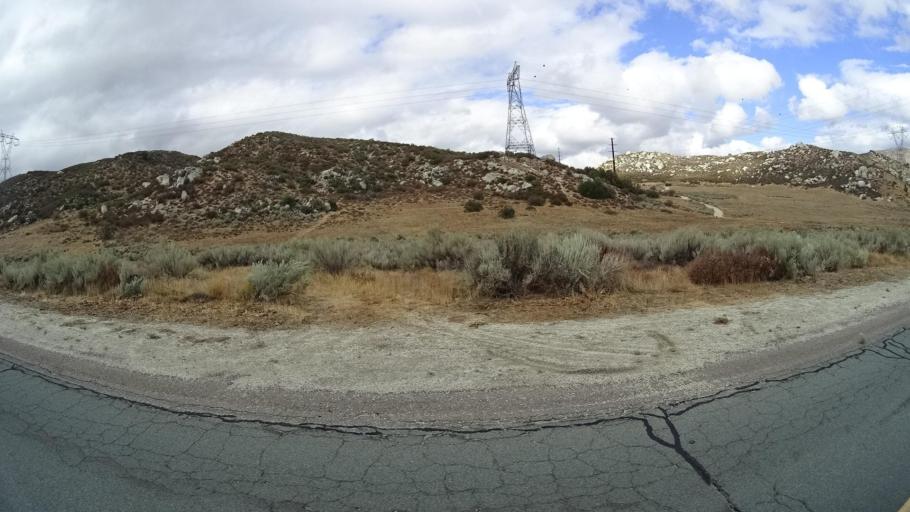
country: US
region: California
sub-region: San Diego County
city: Campo
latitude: 32.7156
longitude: -116.4298
